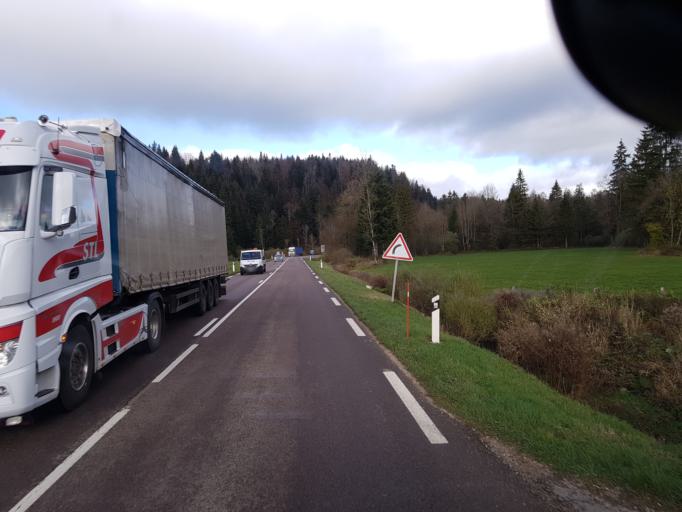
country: FR
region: Franche-Comte
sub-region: Departement du Jura
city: Champagnole
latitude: 46.6404
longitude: 5.9412
